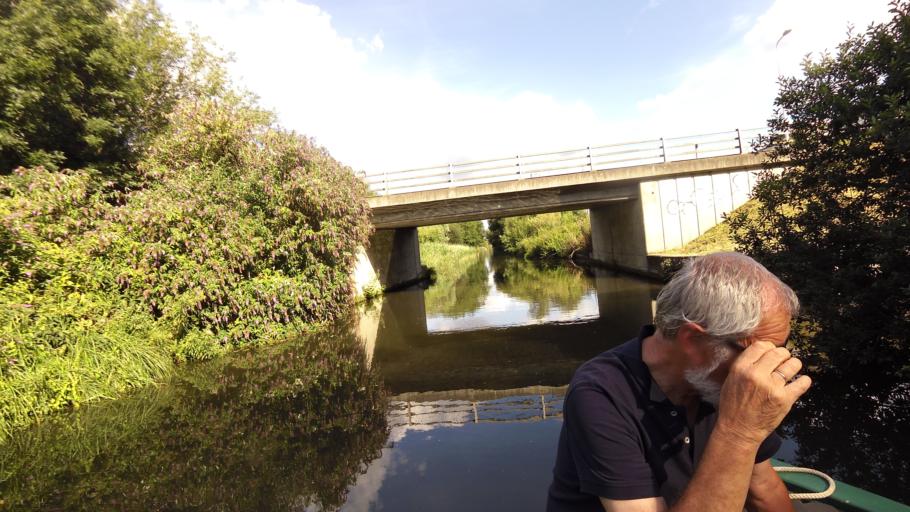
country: GB
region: England
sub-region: West Berkshire
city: Greenham
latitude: 51.4012
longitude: -1.2966
